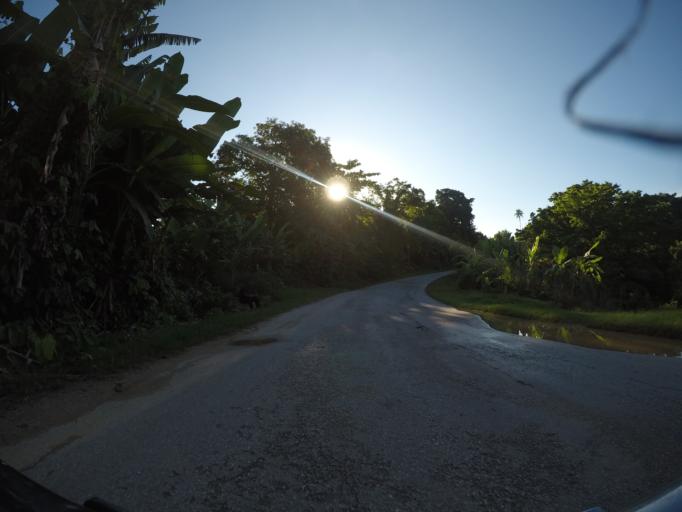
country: TZ
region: Pemba South
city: Mtambile
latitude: -5.3806
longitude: 39.6961
